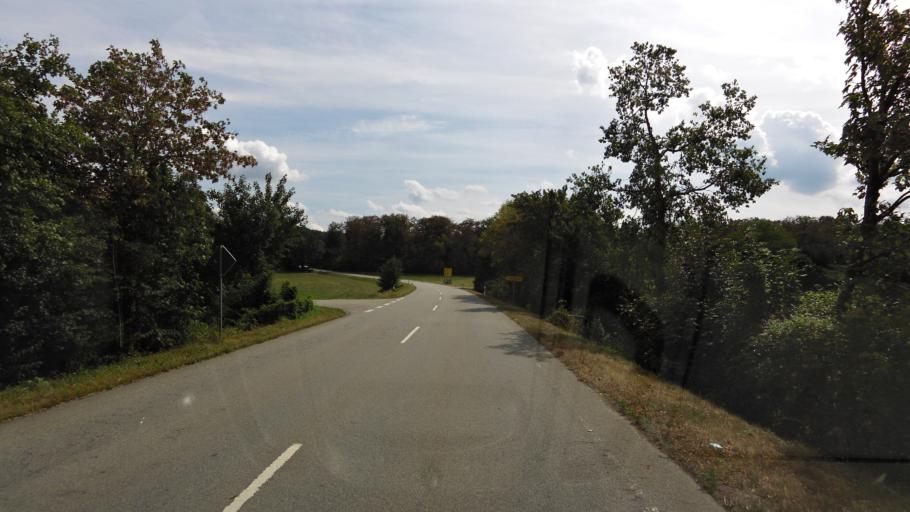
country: DE
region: Bavaria
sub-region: Upper Bavaria
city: Unterneukirchen
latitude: 48.1397
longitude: 12.6302
